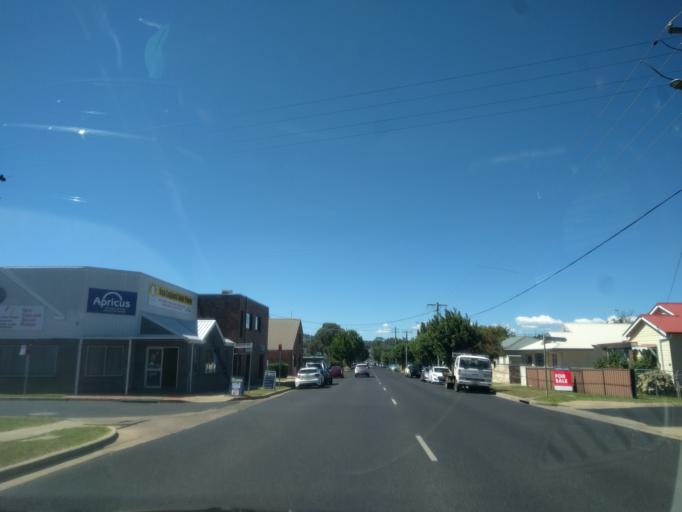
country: AU
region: New South Wales
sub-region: Armidale Dumaresq
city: Armidale
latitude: -30.5157
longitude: 151.6713
